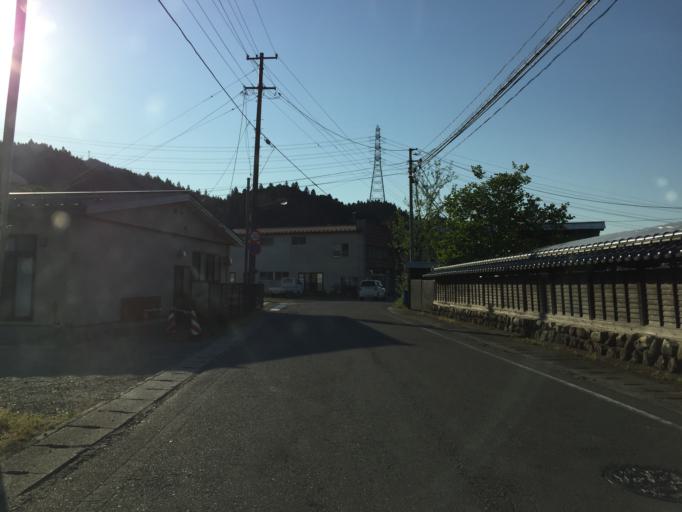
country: JP
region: Ibaraki
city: Daigo
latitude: 36.9410
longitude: 140.4417
